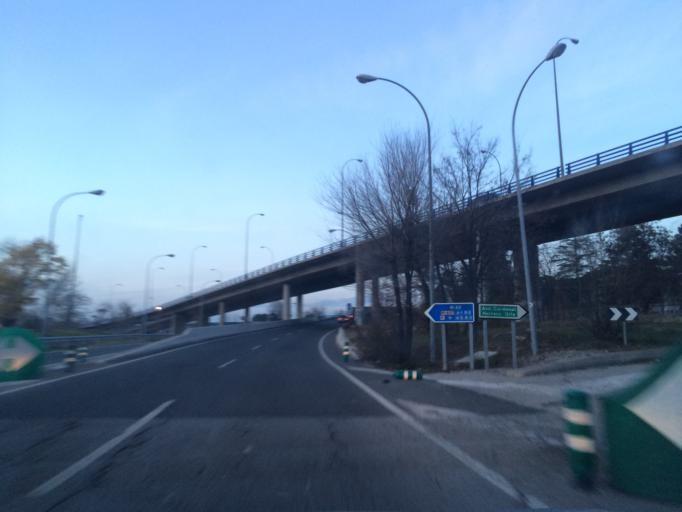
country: ES
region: Madrid
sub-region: Provincia de Madrid
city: Fuencarral-El Pardo
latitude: 40.4748
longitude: -3.7506
